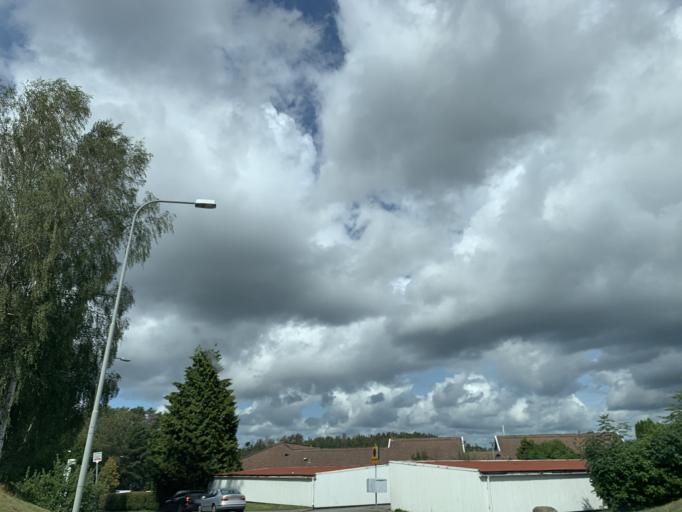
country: SE
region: Vaestra Goetaland
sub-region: Goteborg
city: Eriksbo
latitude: 57.7593
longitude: 12.0646
